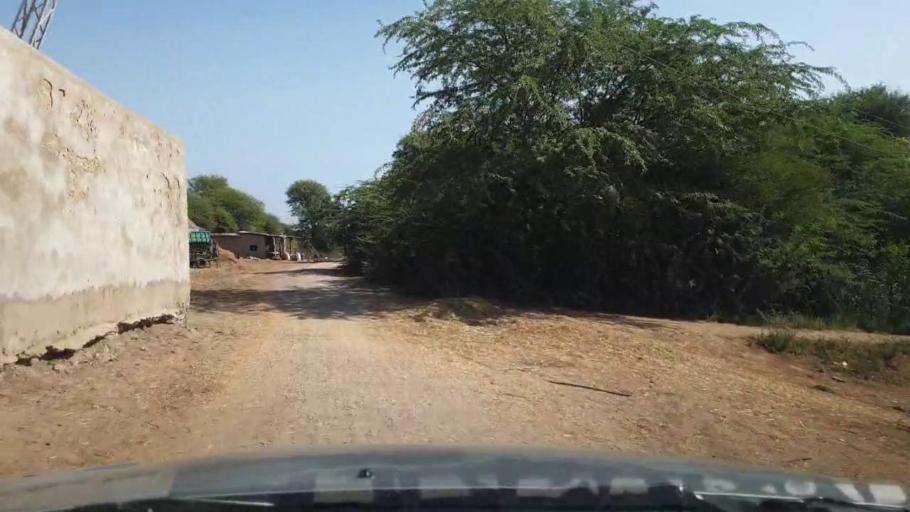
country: PK
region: Sindh
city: Bulri
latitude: 25.0232
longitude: 68.3027
